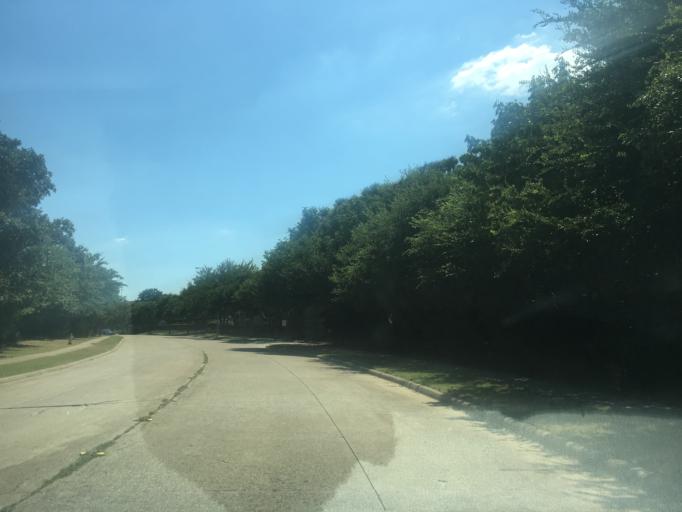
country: US
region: Texas
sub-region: Denton County
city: Lewisville
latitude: 33.0089
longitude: -96.9888
